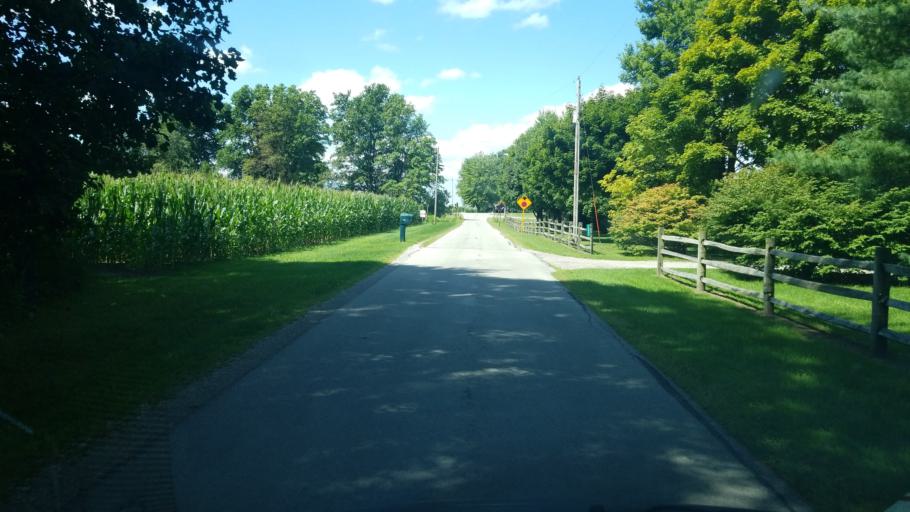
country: US
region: Ohio
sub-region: Lucas County
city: Whitehouse
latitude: 41.4315
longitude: -83.8705
